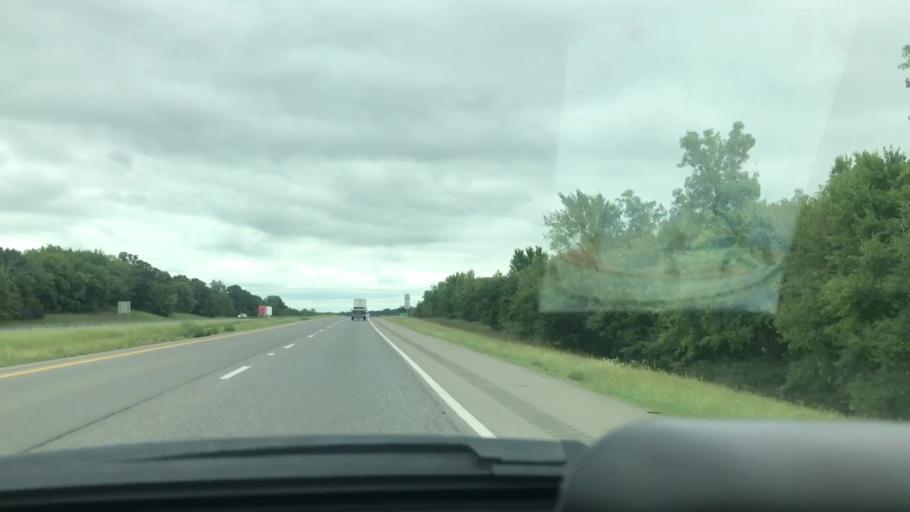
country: US
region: Oklahoma
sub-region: McIntosh County
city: Eufaula
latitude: 35.3706
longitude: -95.5714
